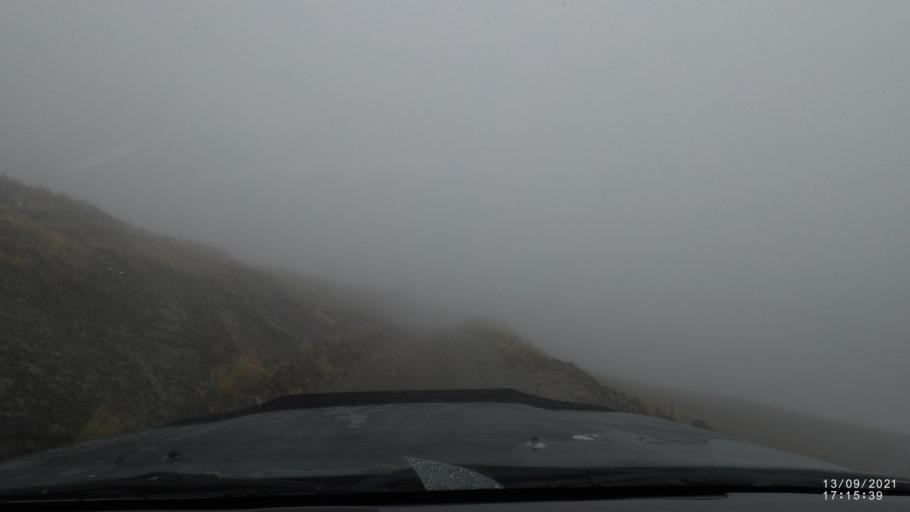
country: BO
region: Cochabamba
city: Colomi
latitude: -17.3440
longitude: -65.7571
